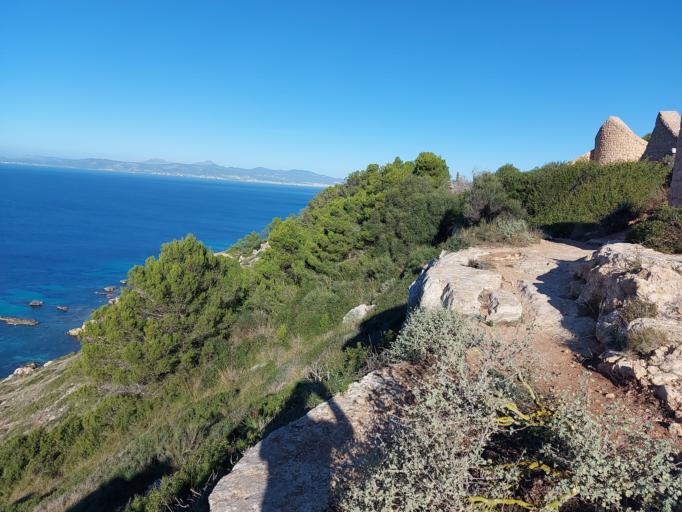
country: ES
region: Balearic Islands
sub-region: Illes Balears
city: s'Arenal
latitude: 39.4409
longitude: 2.7499
